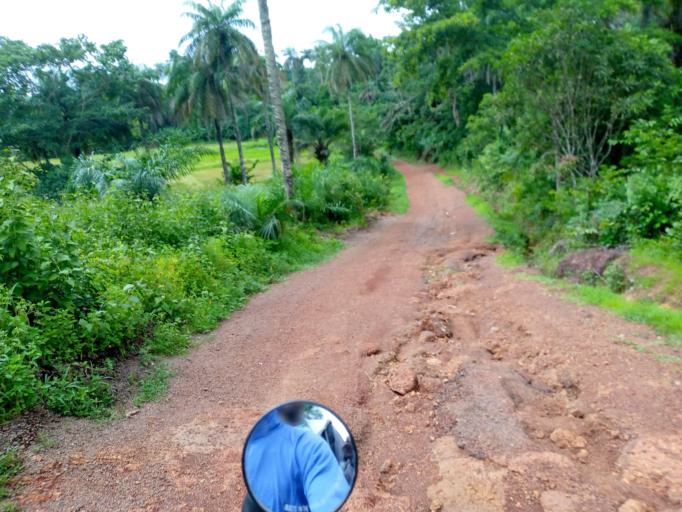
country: SL
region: Northern Province
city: Mange
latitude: 8.9790
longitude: -12.7106
